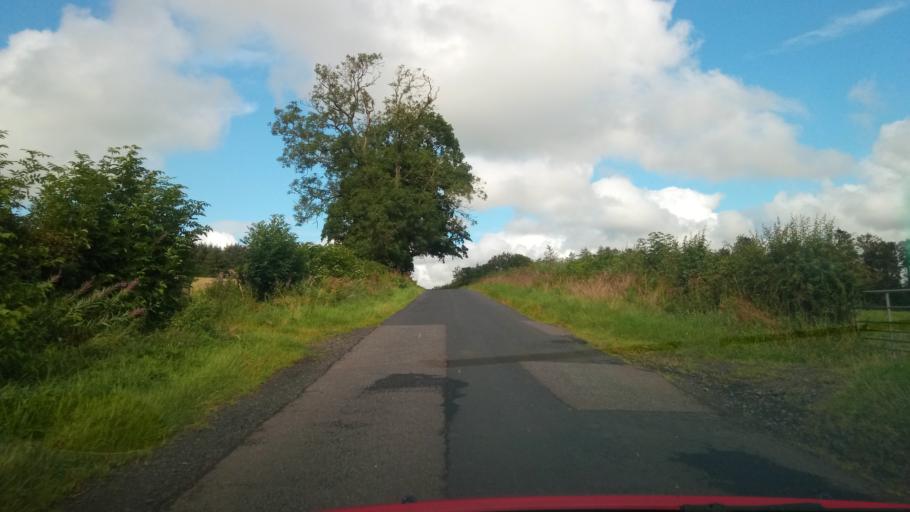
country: GB
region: Scotland
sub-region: The Scottish Borders
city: Earlston
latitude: 55.6392
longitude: -2.6961
